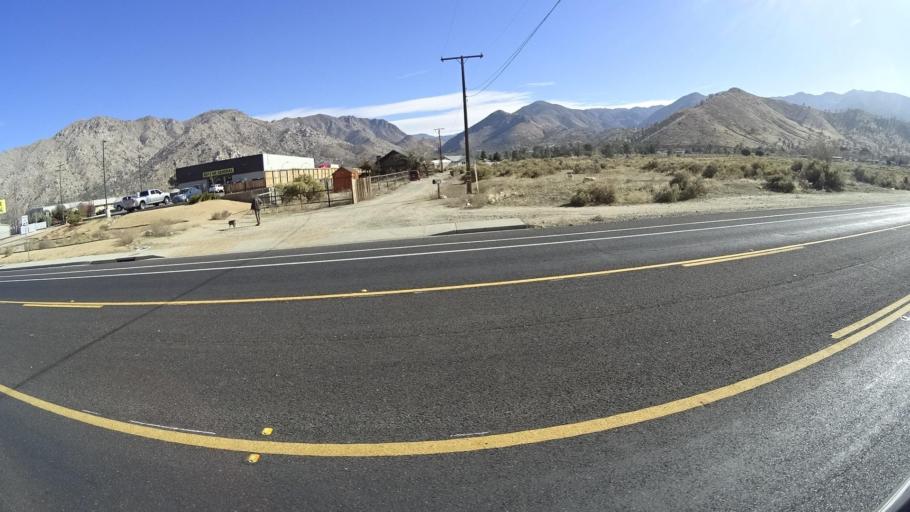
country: US
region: California
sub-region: Kern County
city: Lake Isabella
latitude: 35.6099
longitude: -118.4830
